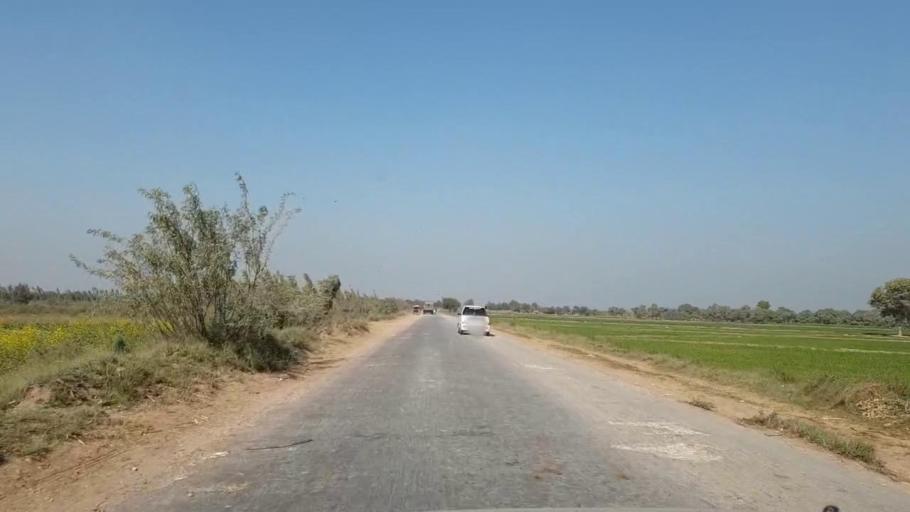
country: PK
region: Sindh
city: Tando Adam
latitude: 25.6545
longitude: 68.5876
